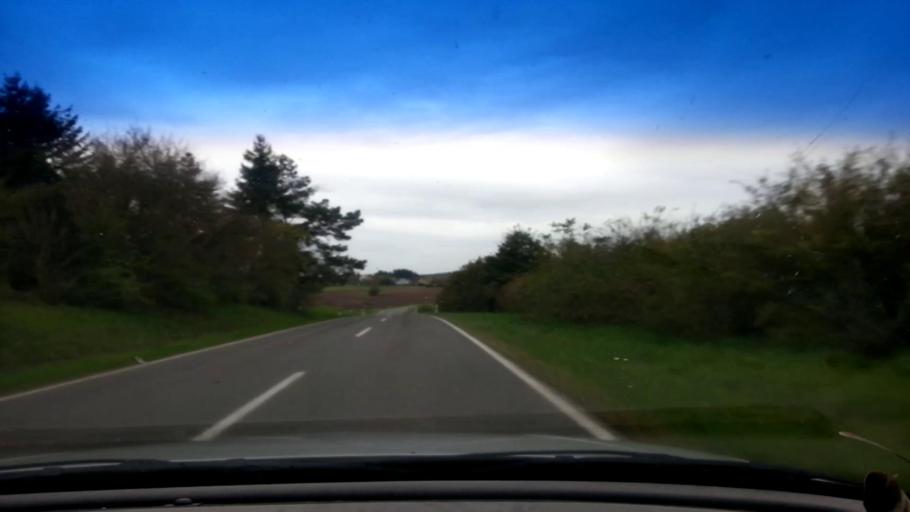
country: DE
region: Bavaria
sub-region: Upper Franconia
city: Priesendorf
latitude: 49.9027
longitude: 10.6865
